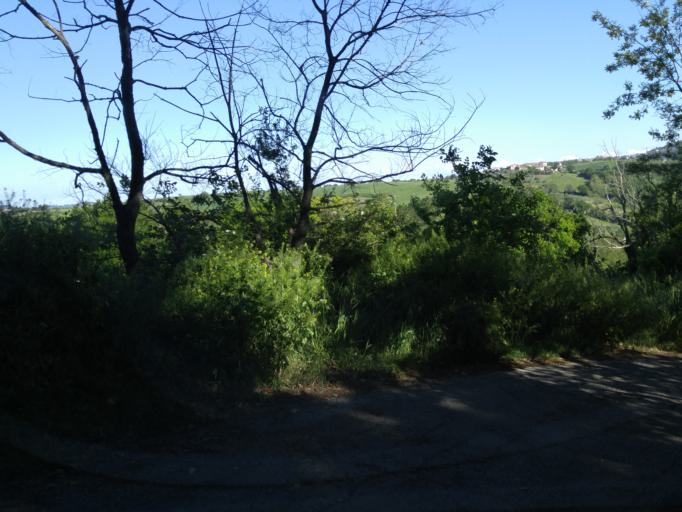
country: IT
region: The Marches
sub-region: Provincia di Pesaro e Urbino
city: Monteciccardo
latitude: 43.8246
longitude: 12.8355
